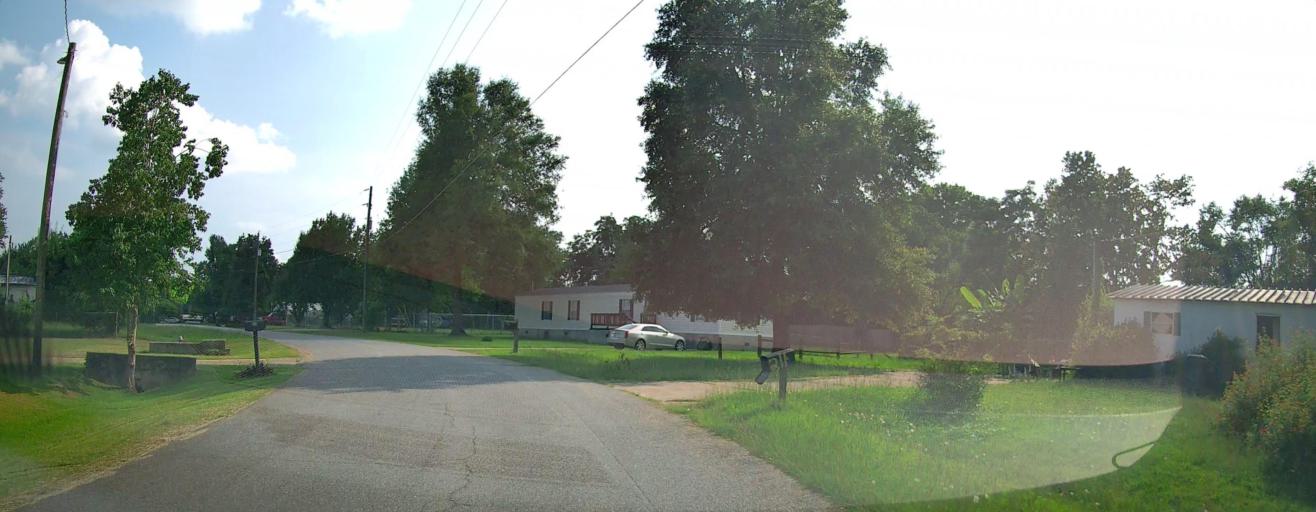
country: US
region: Georgia
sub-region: Houston County
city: Centerville
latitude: 32.6470
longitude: -83.6858
